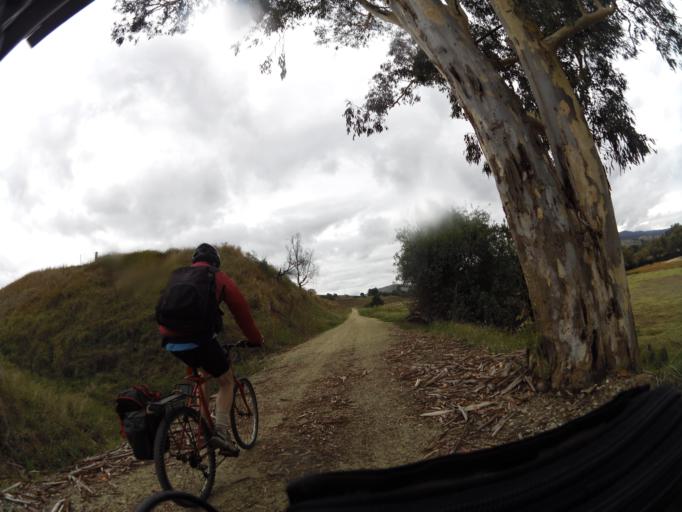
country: AU
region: New South Wales
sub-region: Albury Municipality
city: East Albury
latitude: -36.1920
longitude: 147.2985
